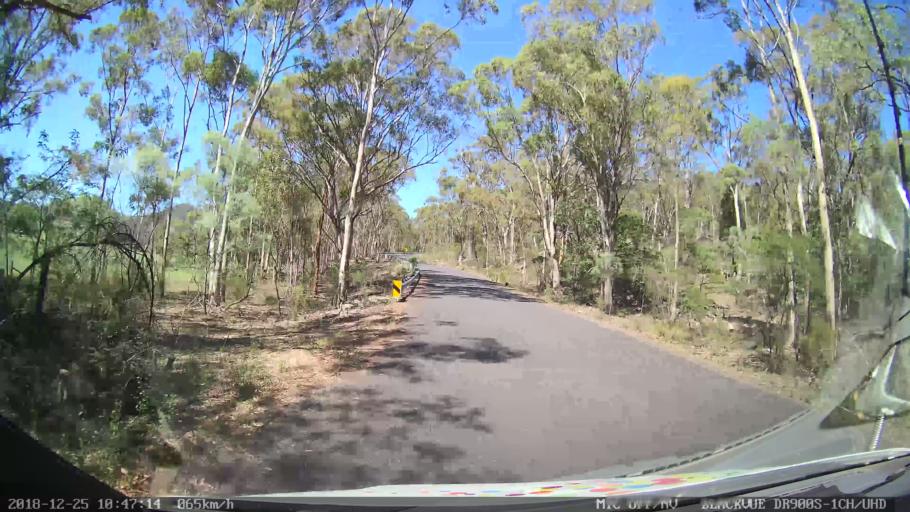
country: AU
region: New South Wales
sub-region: Upper Hunter Shire
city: Merriwa
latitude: -32.4466
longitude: 150.2780
